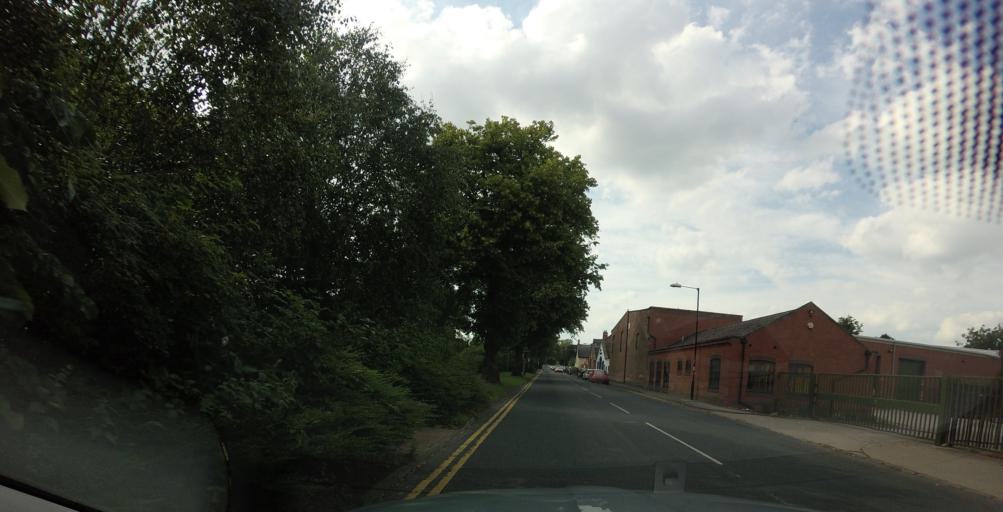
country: GB
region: England
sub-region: North Yorkshire
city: Ripon
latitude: 54.1320
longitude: -1.5158
